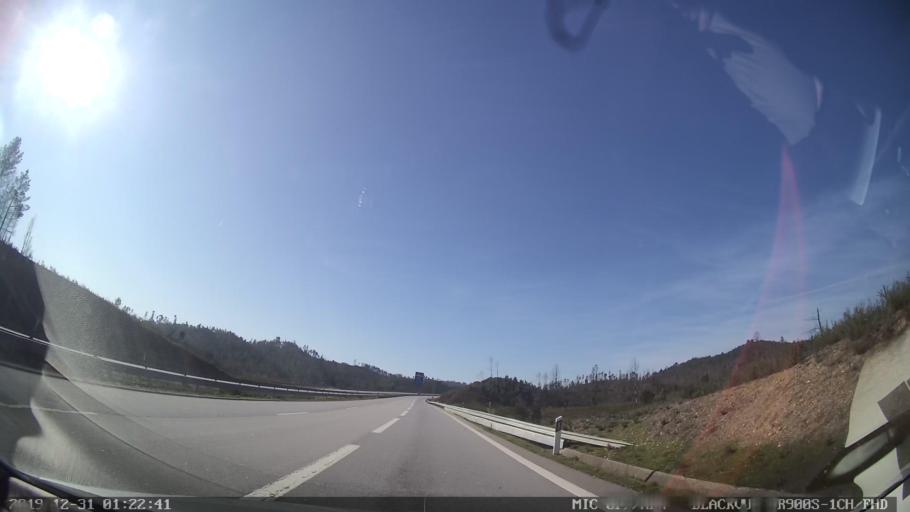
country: PT
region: Santarem
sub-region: Macao
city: Macao
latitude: 39.5216
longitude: -7.9864
